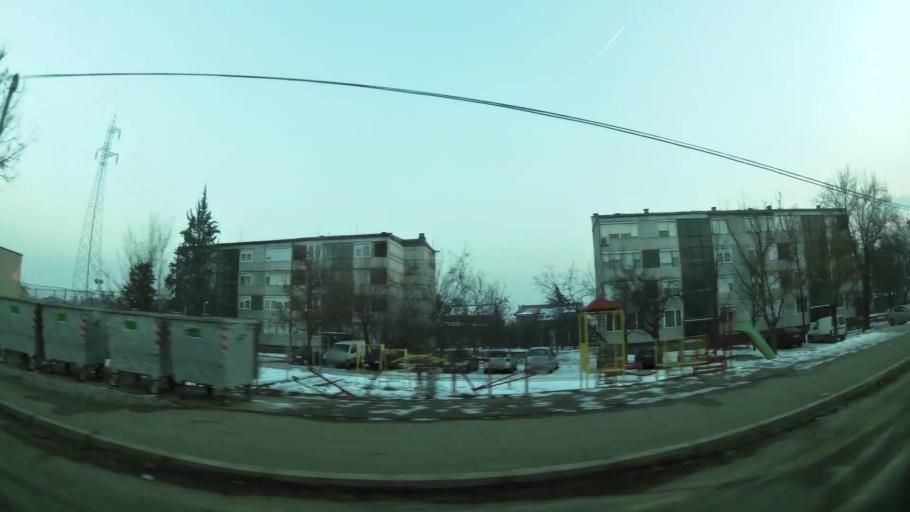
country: MK
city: Creshevo
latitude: 42.0068
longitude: 21.5044
